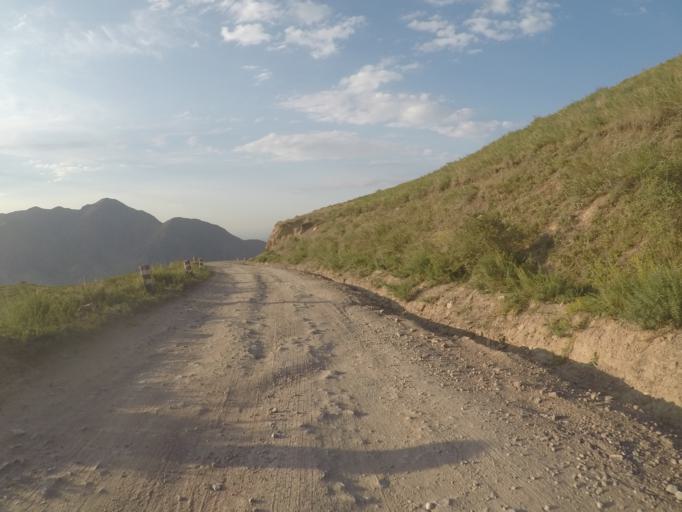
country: KG
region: Chuy
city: Bishkek
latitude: 42.6550
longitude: 74.6630
